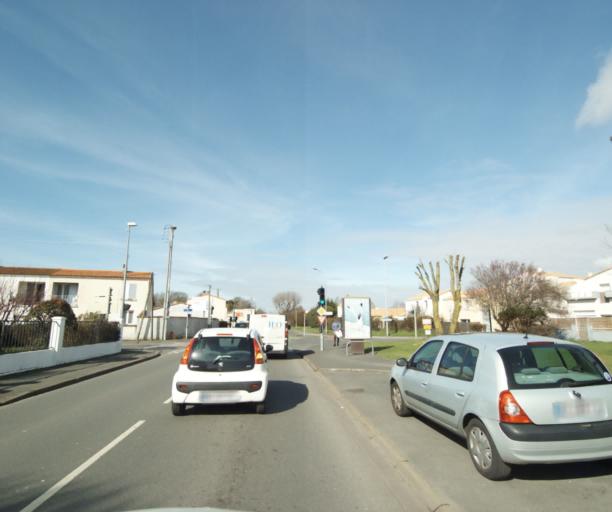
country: FR
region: Poitou-Charentes
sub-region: Departement de la Charente-Maritime
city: La Rochelle
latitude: 46.1714
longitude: -1.1739
